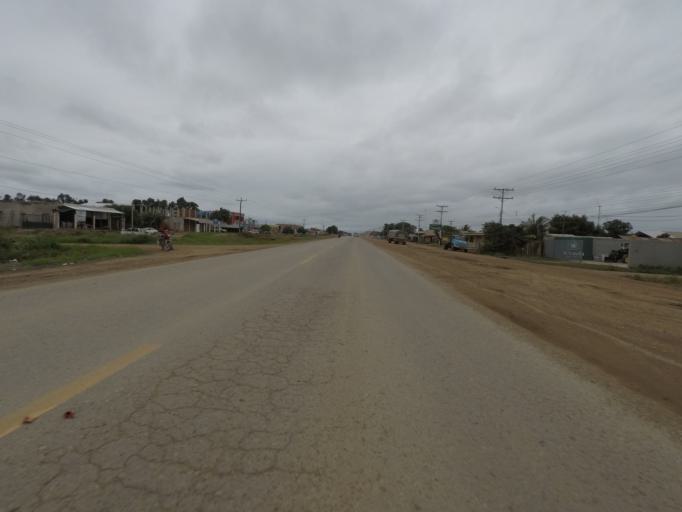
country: BO
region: Santa Cruz
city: Okinawa Numero Uno
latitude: -17.2594
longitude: -62.5554
